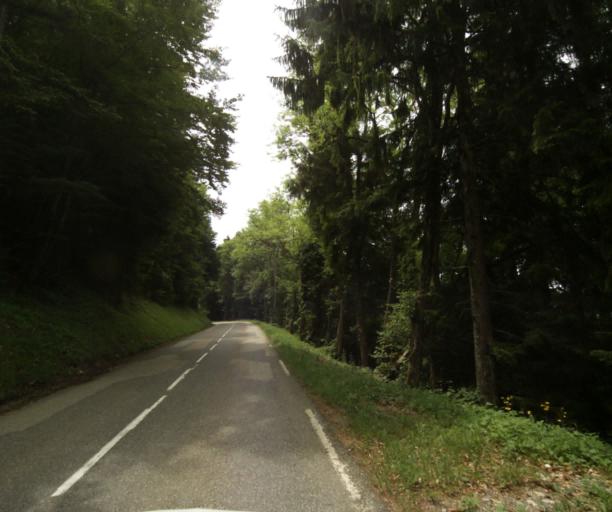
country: FR
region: Rhone-Alpes
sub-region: Departement de la Haute-Savoie
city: Perrignier
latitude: 46.2853
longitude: 6.4600
